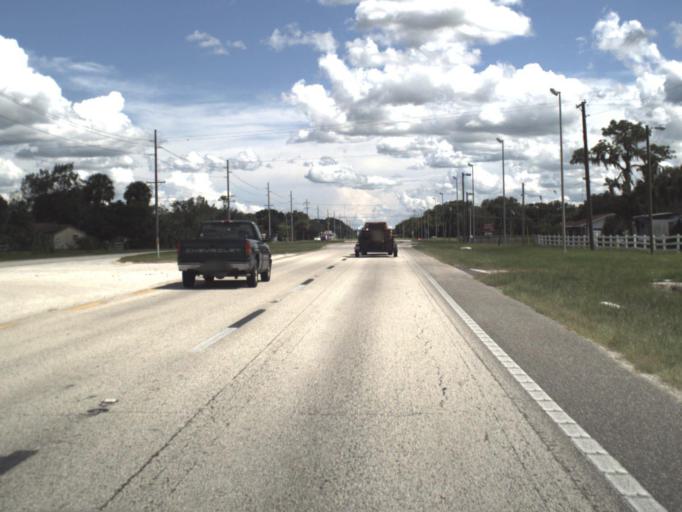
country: US
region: Florida
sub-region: Polk County
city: Willow Oak
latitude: 27.9178
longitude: -82.0242
